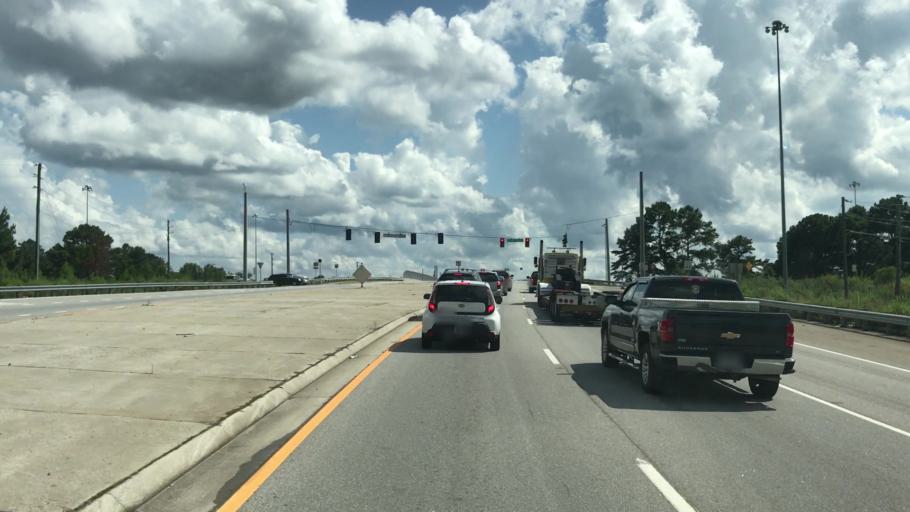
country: US
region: Georgia
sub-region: Newton County
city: Covington
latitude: 33.6148
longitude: -83.8240
